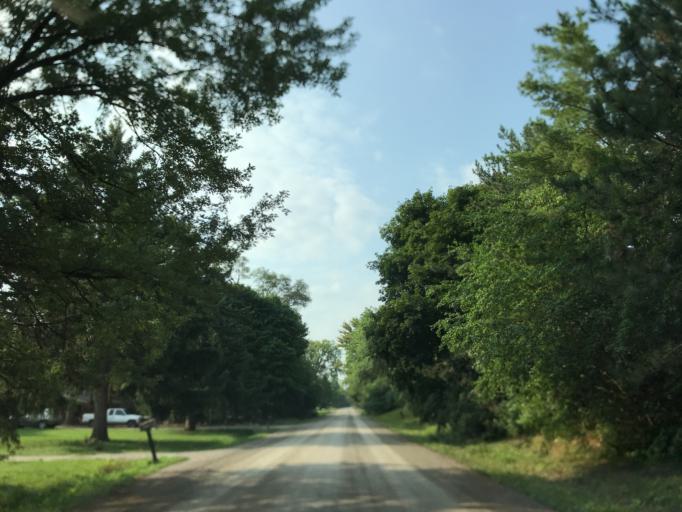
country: US
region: Michigan
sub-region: Washtenaw County
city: Ann Arbor
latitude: 42.2514
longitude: -83.6794
